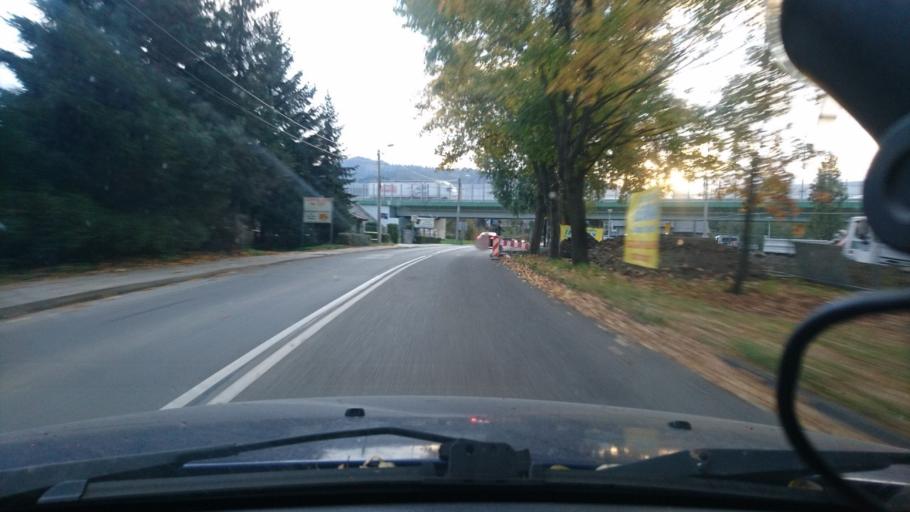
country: PL
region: Silesian Voivodeship
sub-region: Bielsko-Biala
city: Bielsko-Biala
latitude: 49.8020
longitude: 19.0794
